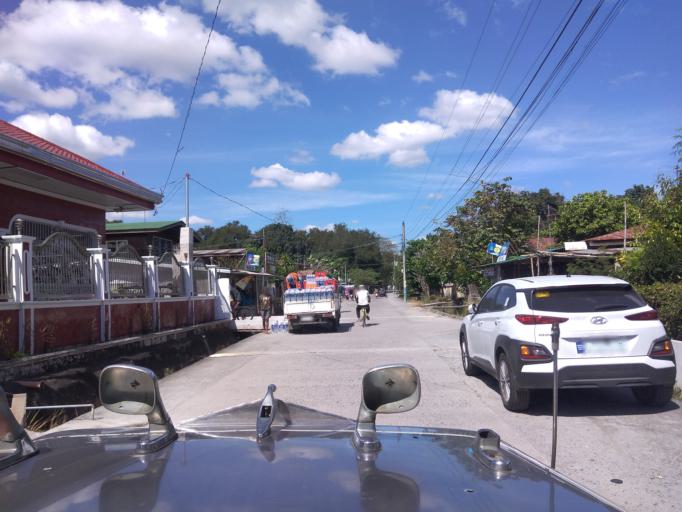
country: PH
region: Central Luzon
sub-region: Province of Pampanga
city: Santa Rita
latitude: 15.0034
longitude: 120.6026
